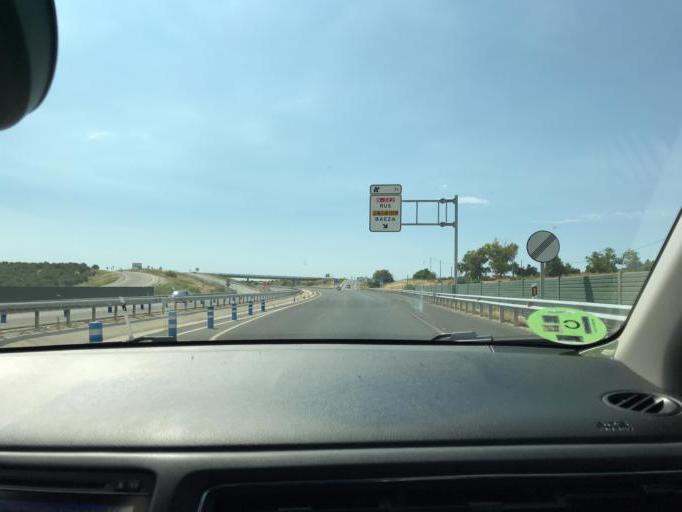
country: ES
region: Andalusia
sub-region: Provincia de Jaen
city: Ubeda
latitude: 38.0214
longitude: -3.4155
